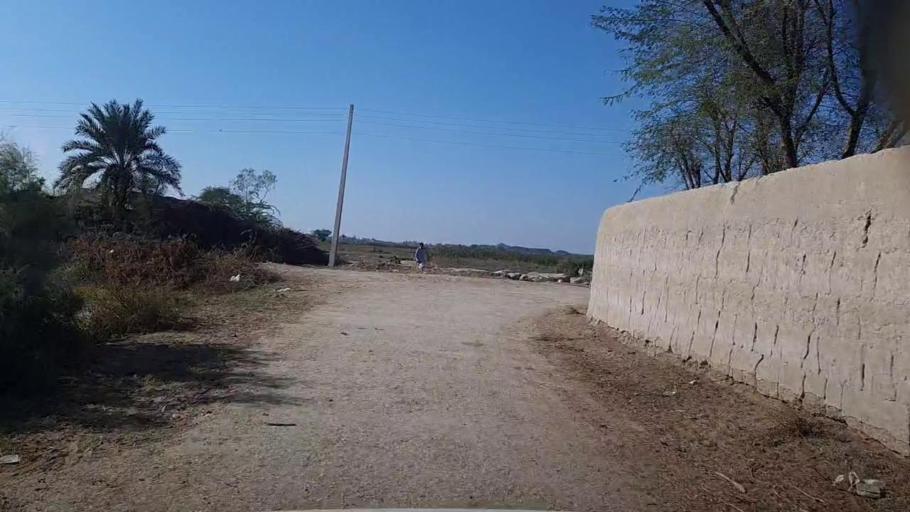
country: PK
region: Sindh
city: Khairpur
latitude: 27.9560
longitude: 69.7506
